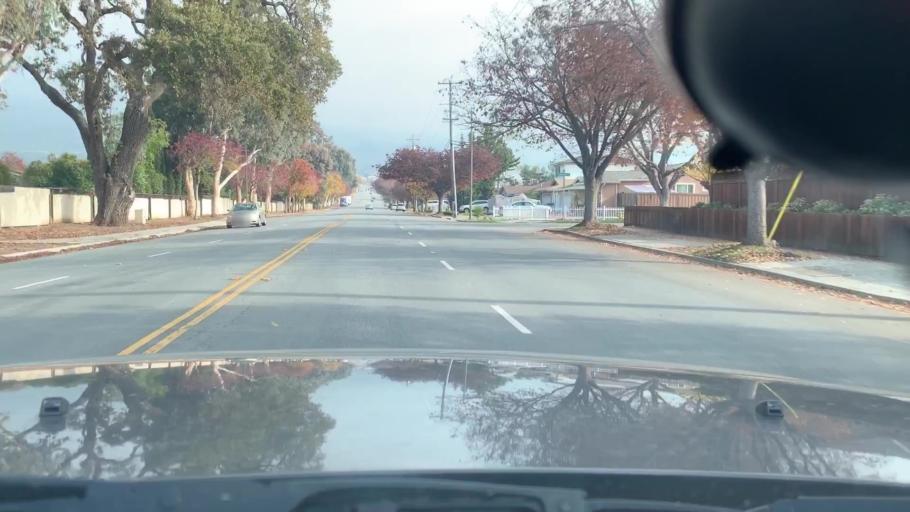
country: US
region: California
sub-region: Santa Clara County
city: Alum Rock
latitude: 37.3248
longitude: -121.7923
